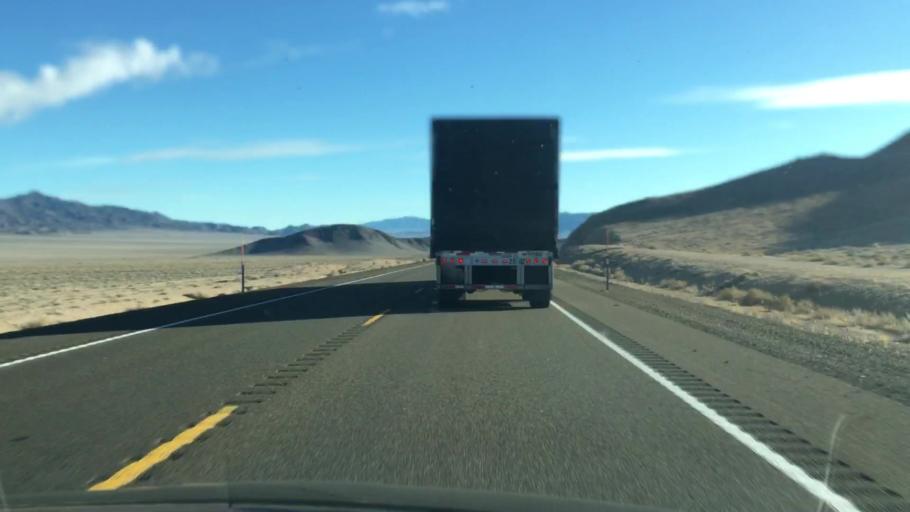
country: US
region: Nevada
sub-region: Nye County
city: Tonopah
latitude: 38.1662
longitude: -117.9544
